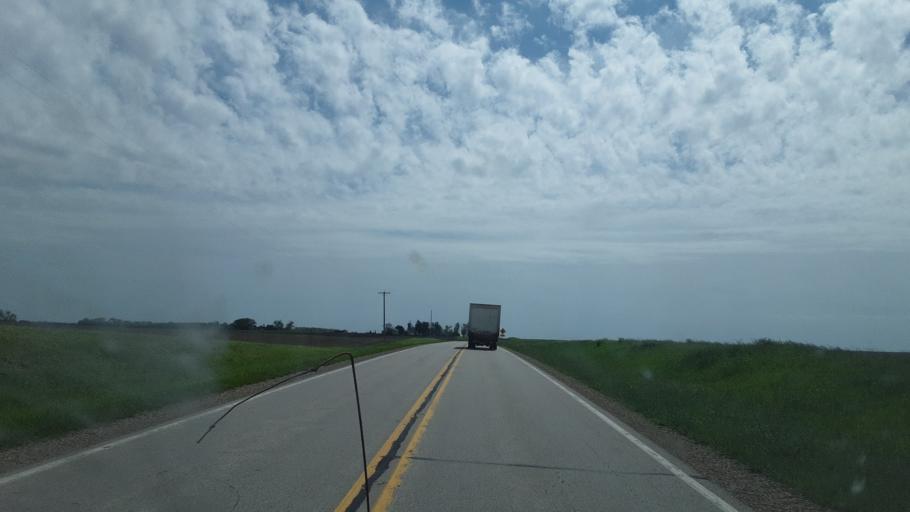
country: US
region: Illinois
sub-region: Logan County
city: Atlanta
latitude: 40.3111
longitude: -89.2387
